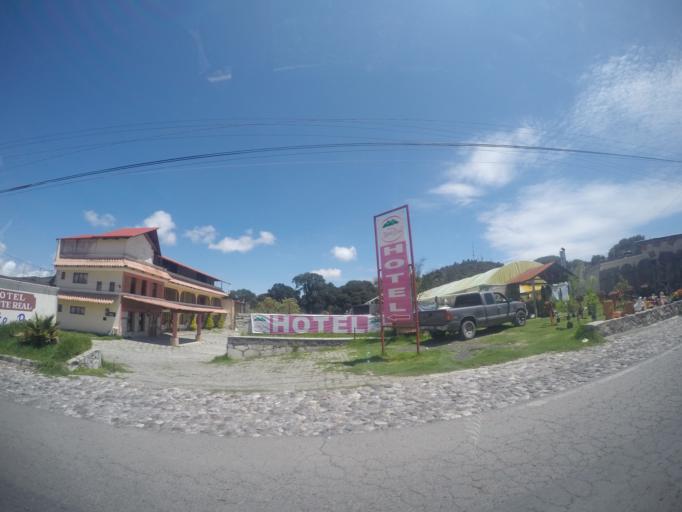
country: MX
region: Hidalgo
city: Mineral del Monte
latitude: 20.1390
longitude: -98.6852
